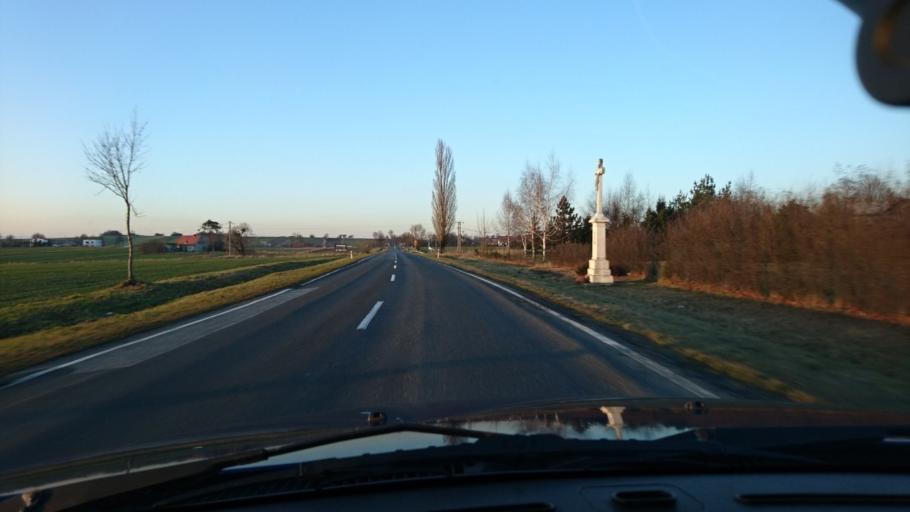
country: PL
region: Silesian Voivodeship
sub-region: Powiat gliwicki
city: Wielowies
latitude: 50.4695
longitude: 18.6105
